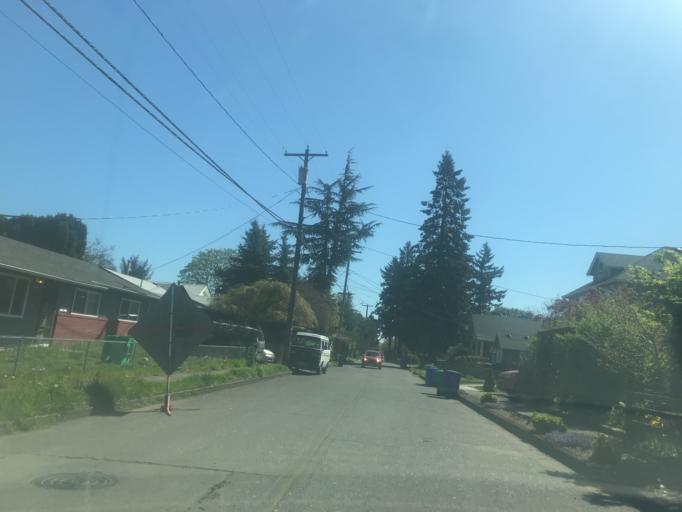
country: US
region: Oregon
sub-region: Multnomah County
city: Lents
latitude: 45.4867
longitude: -122.6013
